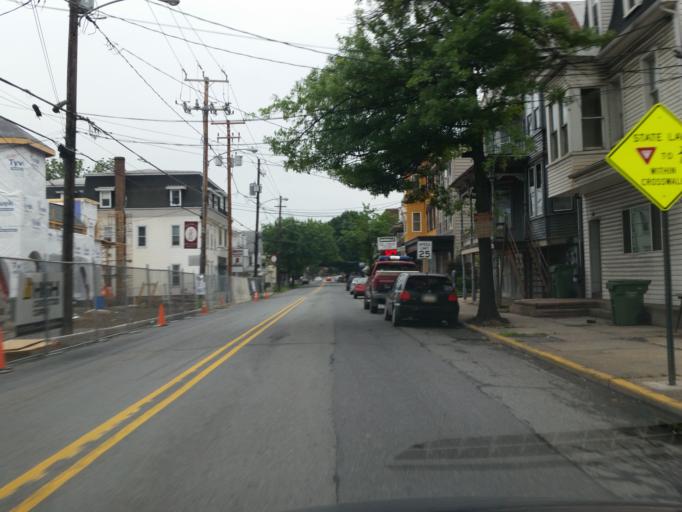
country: US
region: Pennsylvania
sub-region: Schuylkill County
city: Pine Grove
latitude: 40.5521
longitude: -76.3858
